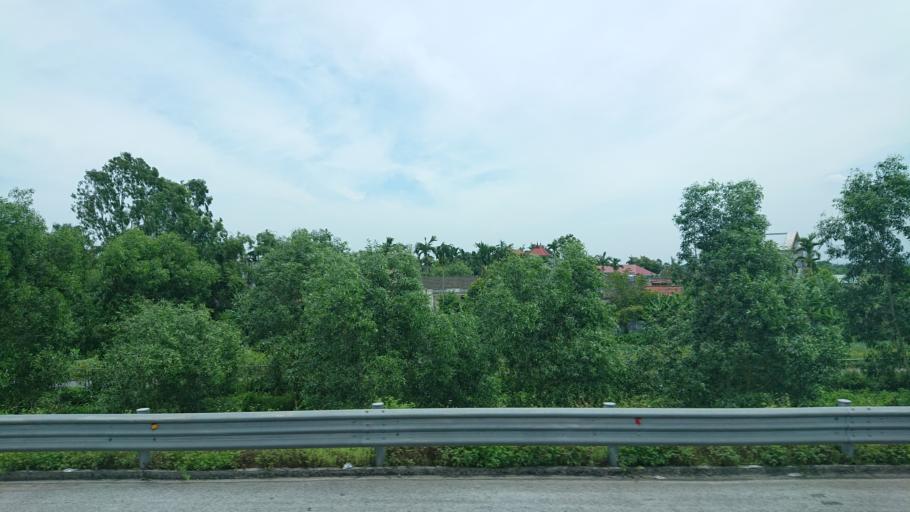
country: VN
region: Hai Phong
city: Nui Doi
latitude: 20.7676
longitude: 106.6384
